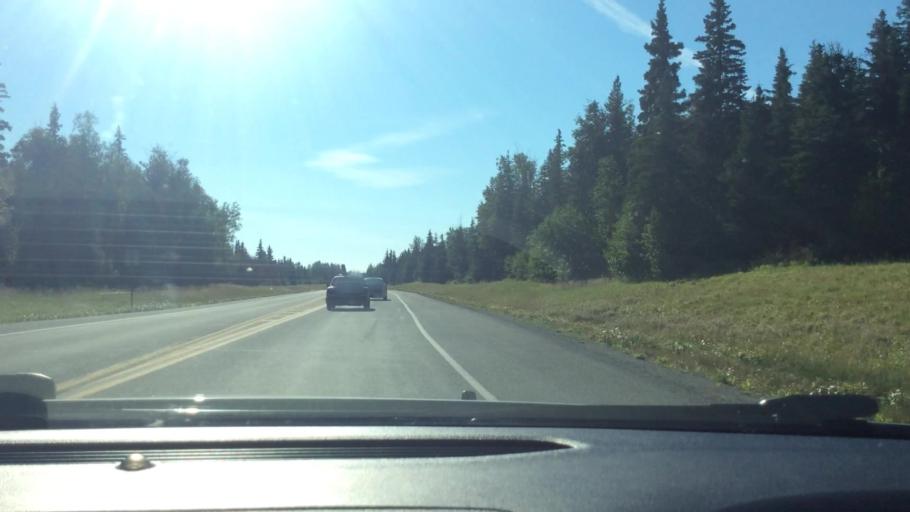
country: US
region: Alaska
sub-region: Anchorage Municipality
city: Elmendorf Air Force Base
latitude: 61.2400
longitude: -149.7108
